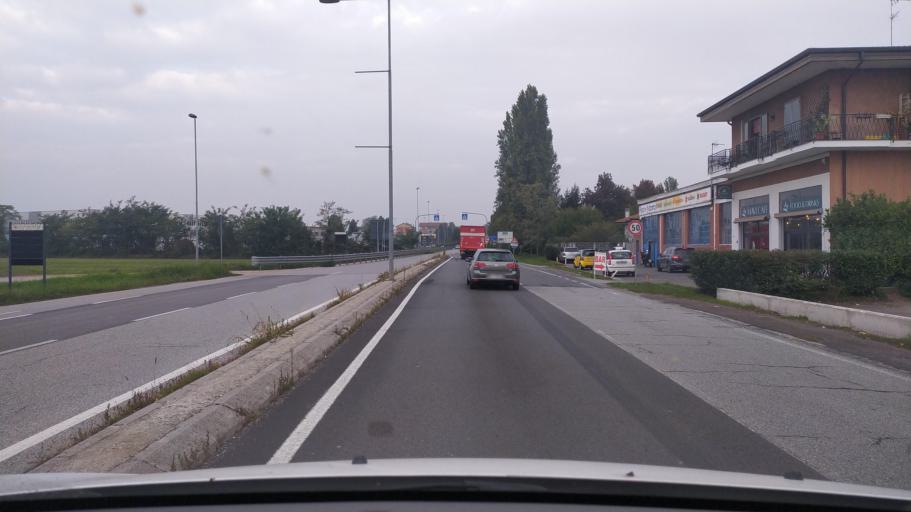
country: IT
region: Lombardy
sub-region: Citta metropolitana di Milano
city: Vittuone
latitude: 45.4824
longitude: 8.9483
